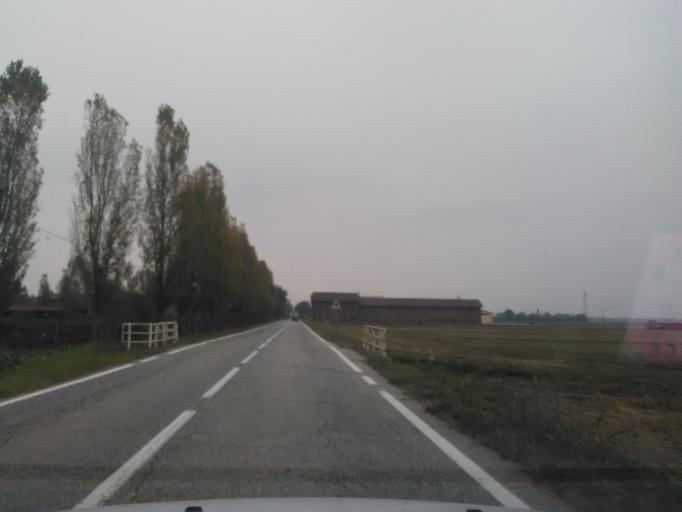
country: IT
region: Piedmont
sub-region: Provincia di Vercelli
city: Fontanetto Po
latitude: 45.2463
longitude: 8.1754
